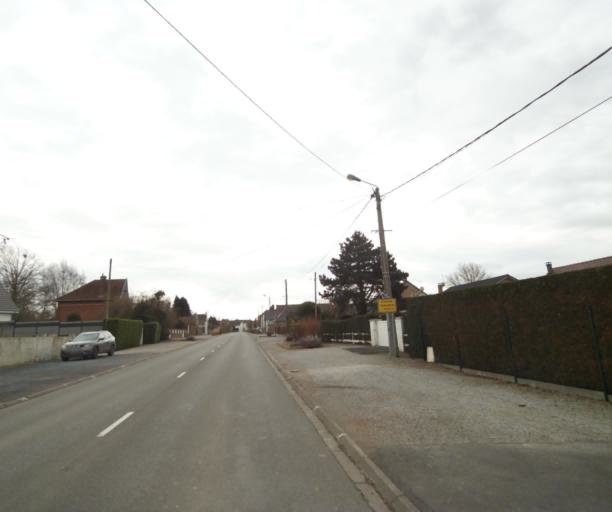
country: FR
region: Nord-Pas-de-Calais
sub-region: Departement du Nord
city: Curgies
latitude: 50.3326
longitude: 3.5952
